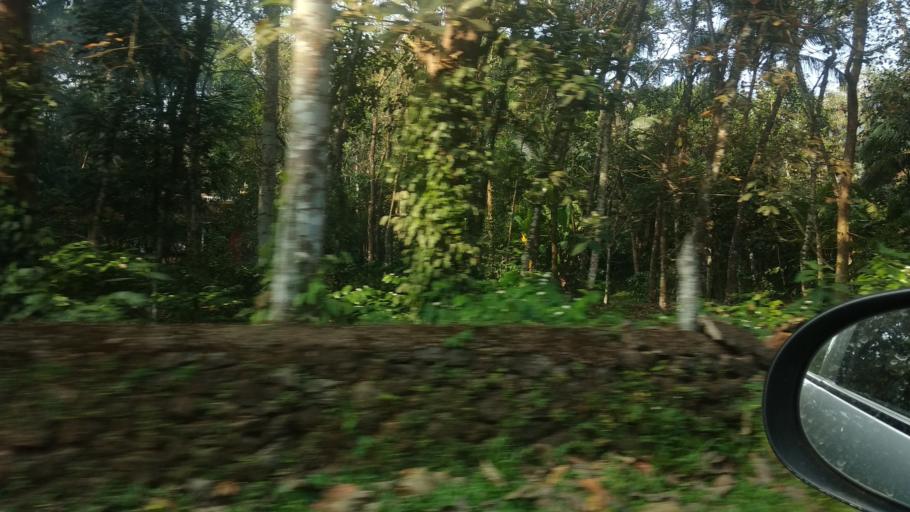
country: IN
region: Kerala
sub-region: Kottayam
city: Changanacheri
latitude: 9.5039
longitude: 76.6821
